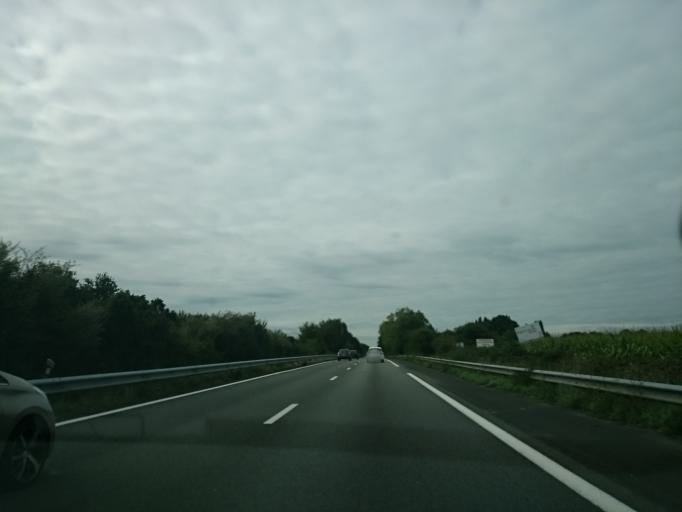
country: FR
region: Pays de la Loire
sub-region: Departement de la Loire-Atlantique
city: Jans
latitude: 47.6155
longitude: -1.6351
